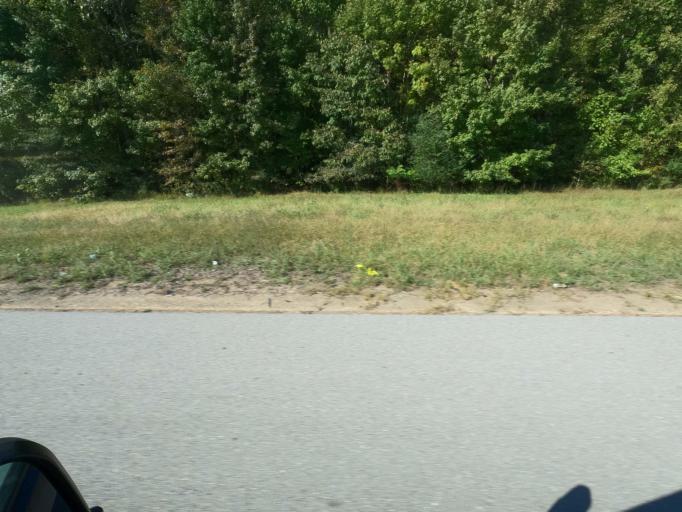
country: US
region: Tennessee
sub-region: Shelby County
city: Arlington
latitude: 35.2653
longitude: -89.6790
